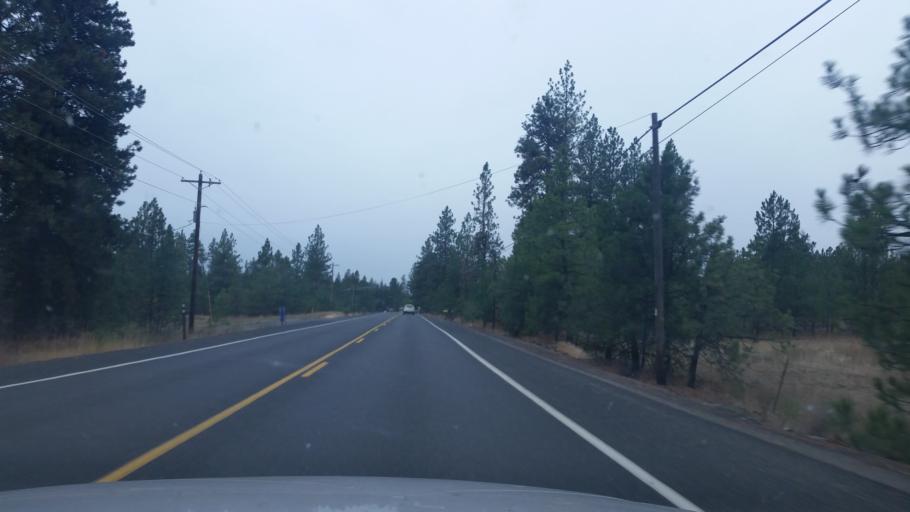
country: US
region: Washington
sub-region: Spokane County
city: Cheney
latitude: 47.5060
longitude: -117.5526
